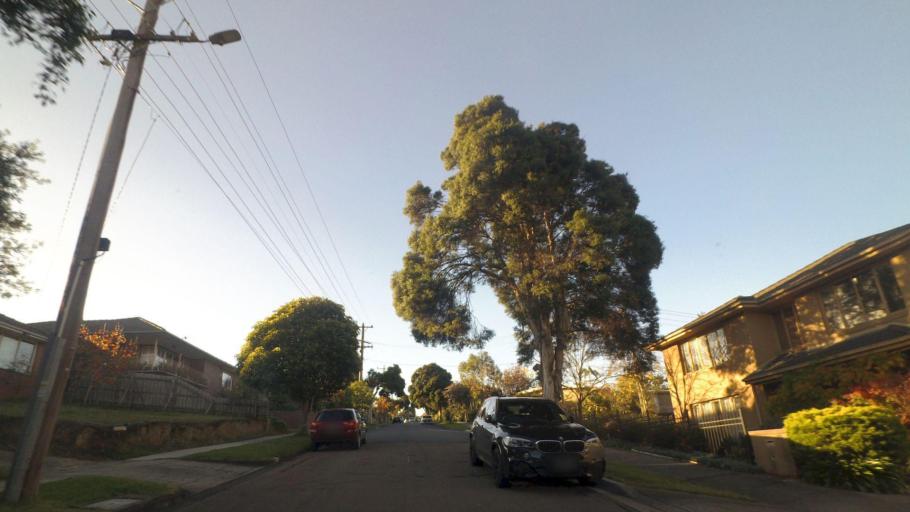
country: AU
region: Victoria
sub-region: Manningham
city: Doncaster East
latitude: -37.7943
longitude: 145.1563
